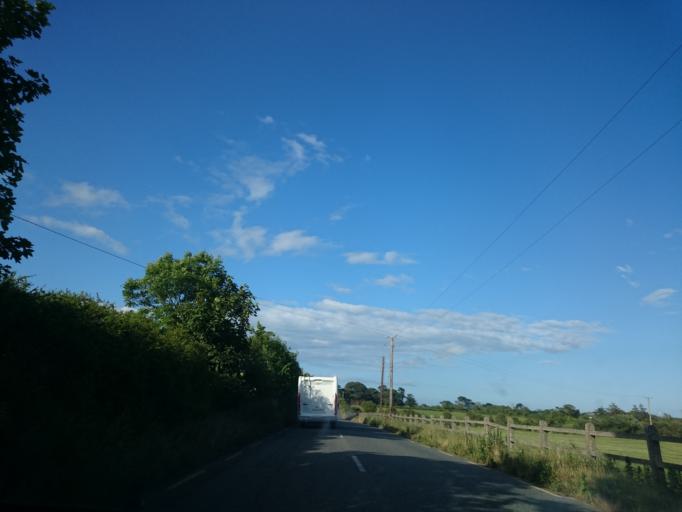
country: IE
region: Leinster
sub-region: Loch Garman
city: Loch Garman
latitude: 52.2113
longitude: -6.5334
